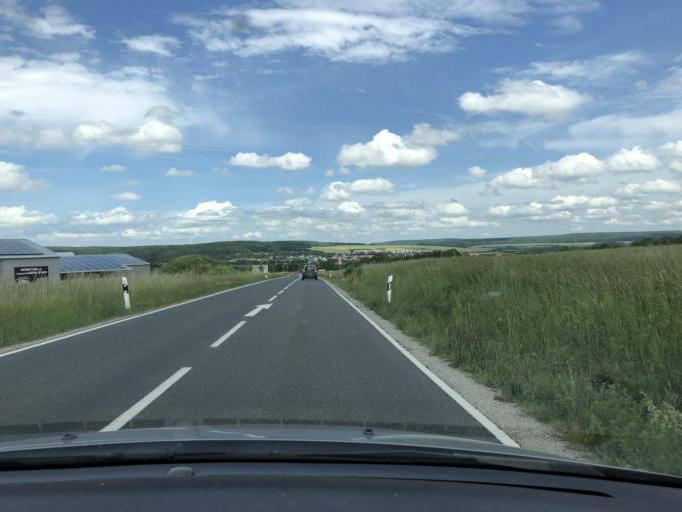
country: DE
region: Thuringia
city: Kefferhausen
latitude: 51.3060
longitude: 10.2948
